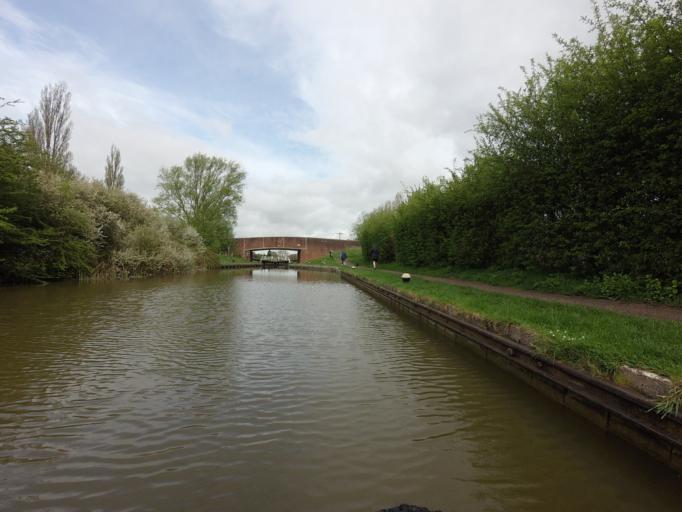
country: GB
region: England
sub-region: Milton Keynes
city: Water Eaton
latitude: 51.9460
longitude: -0.7027
